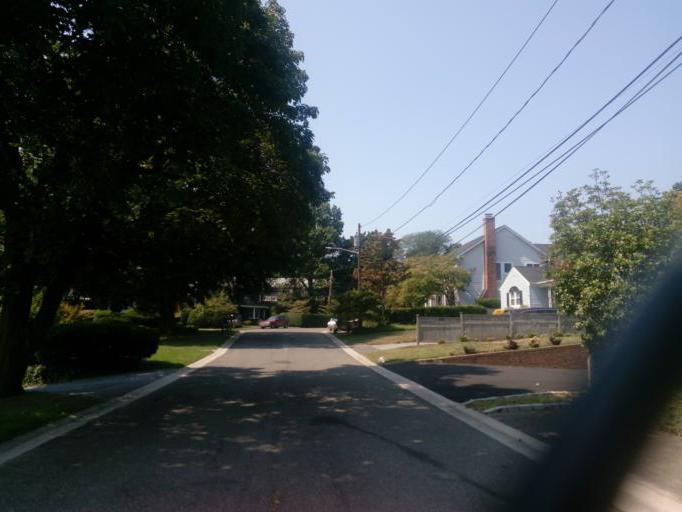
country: US
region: New York
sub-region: Nassau County
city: Locust Valley
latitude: 40.8791
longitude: -73.5932
